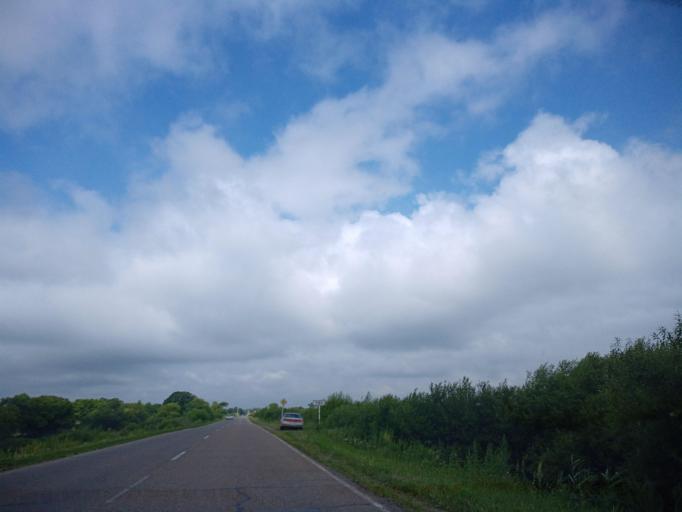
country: RU
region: Primorskiy
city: Dal'nerechensk
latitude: 45.9343
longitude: 133.8283
